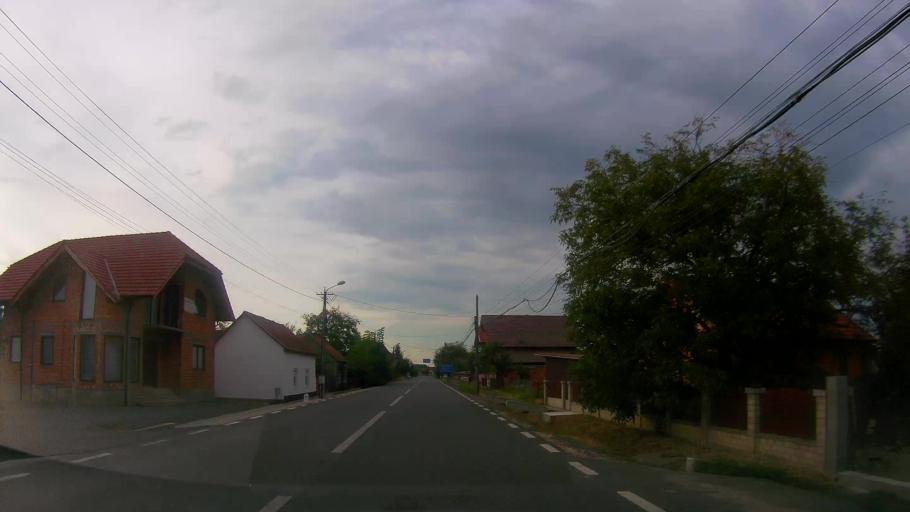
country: RO
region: Satu Mare
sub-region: Comuna Halmeu
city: Halmeu
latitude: 47.9813
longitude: 23.0088
